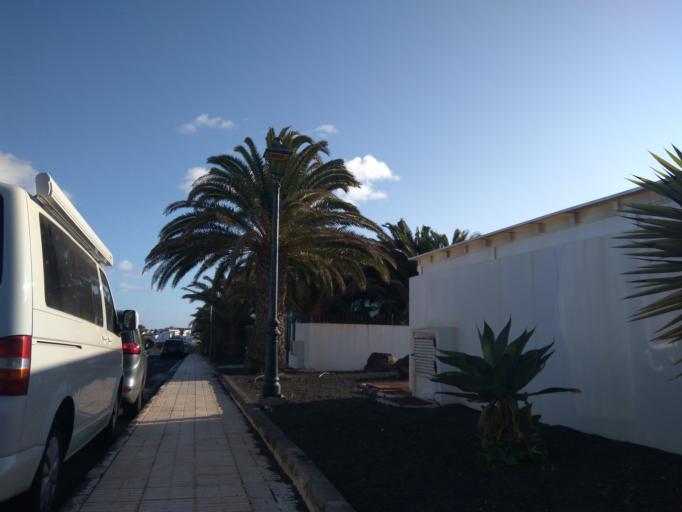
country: ES
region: Canary Islands
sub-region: Provincia de Las Palmas
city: Arrecife
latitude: 29.0069
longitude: -13.4907
